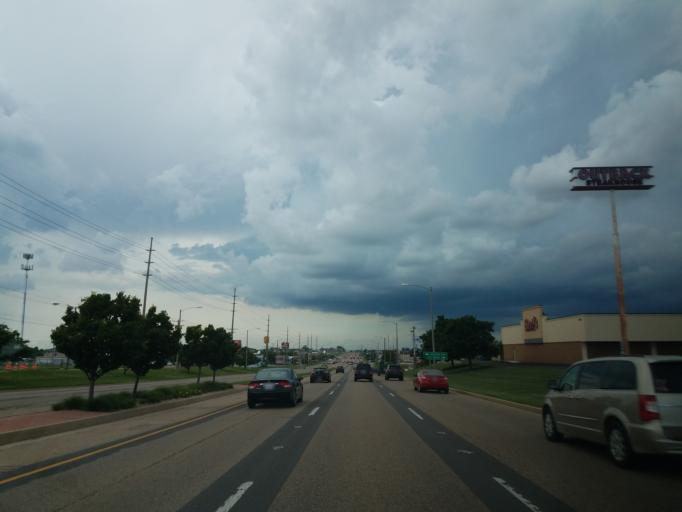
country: US
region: Illinois
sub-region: McLean County
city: Normal
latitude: 40.4983
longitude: -88.9529
